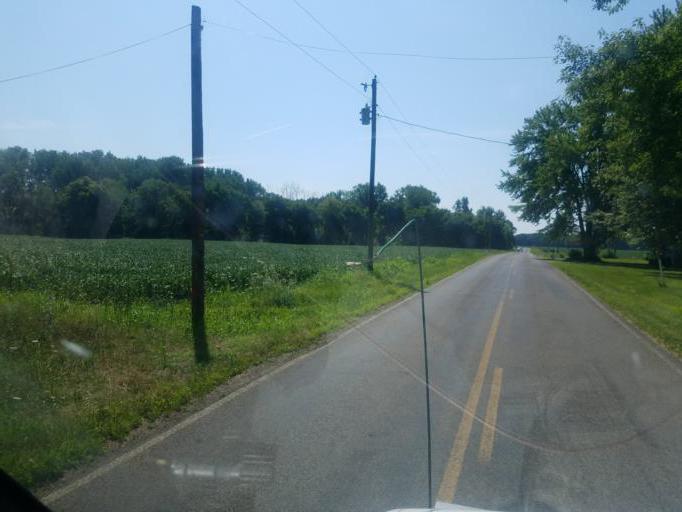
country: US
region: Ohio
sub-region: Champaign County
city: North Lewisburg
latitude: 40.2264
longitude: -83.5250
